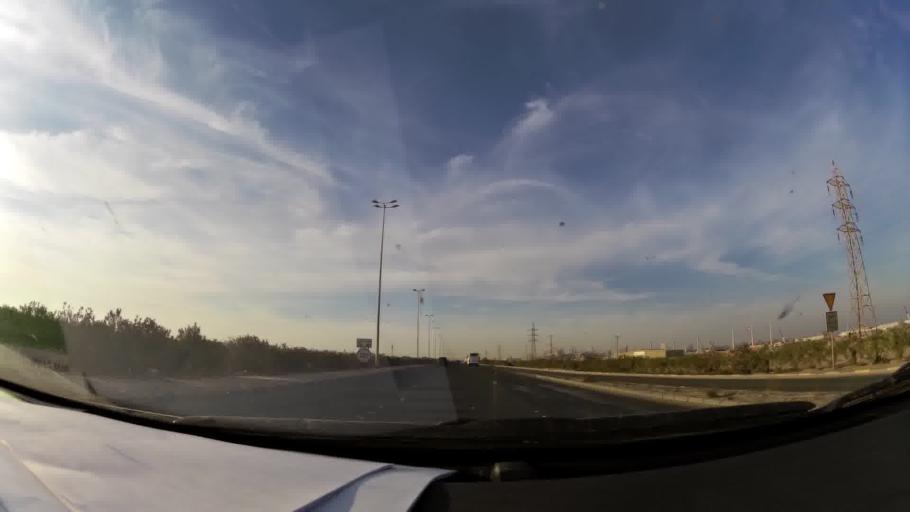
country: KW
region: Al Ahmadi
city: Al Fahahil
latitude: 28.9779
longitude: 48.1576
